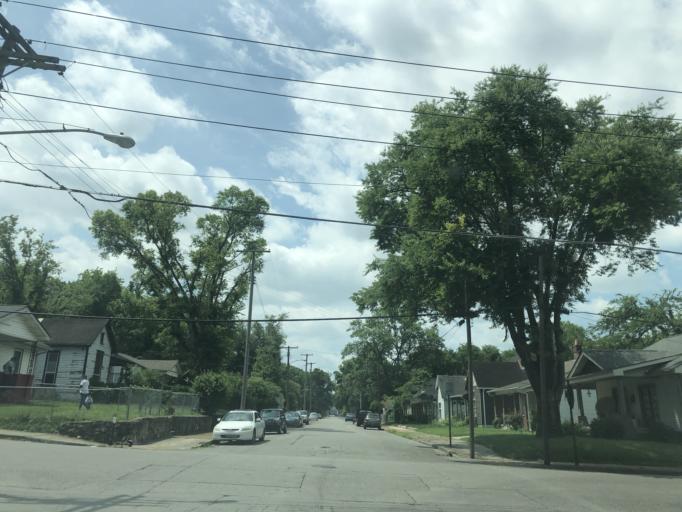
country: US
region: Tennessee
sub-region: Davidson County
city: Nashville
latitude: 36.1920
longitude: -86.7648
